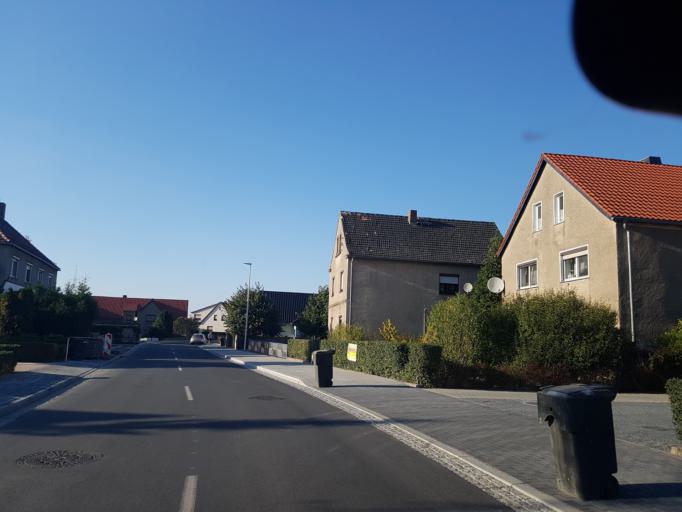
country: DE
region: Saxony
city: Nauwalde
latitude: 51.4227
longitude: 13.4072
